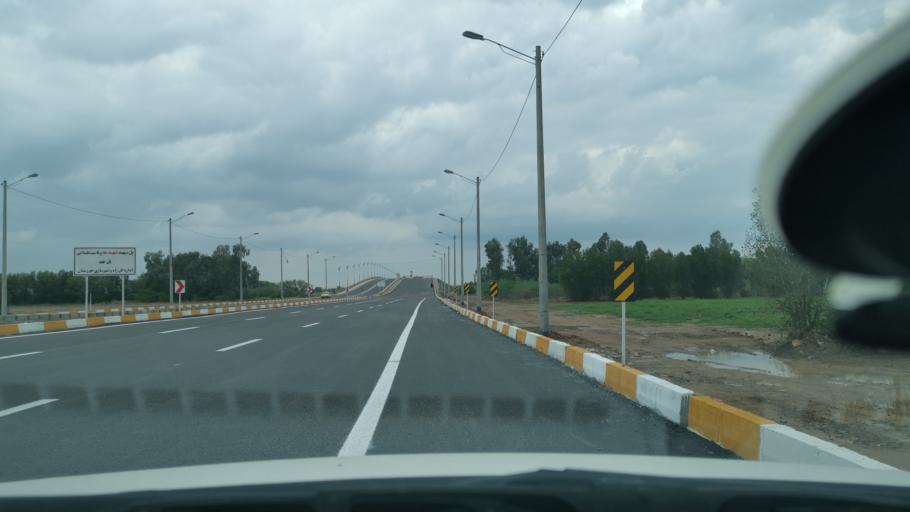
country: IR
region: Khuzestan
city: Ahvaz
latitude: 31.3589
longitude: 48.6854
